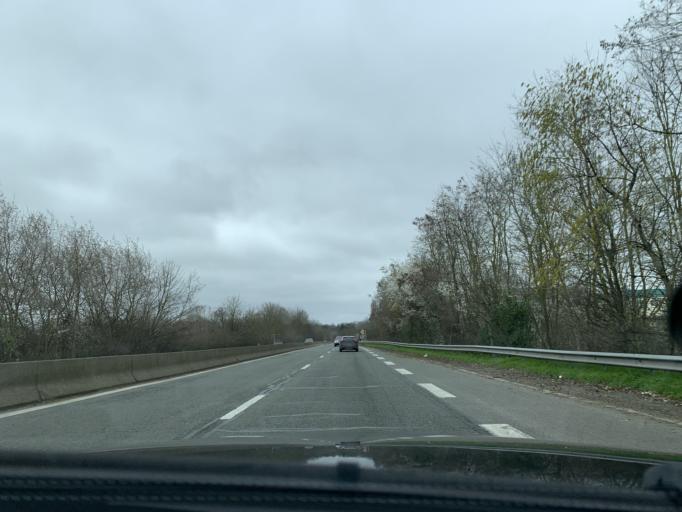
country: FR
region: Ile-de-France
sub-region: Departement du Val-d'Oise
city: Domont
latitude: 49.0320
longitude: 2.3464
